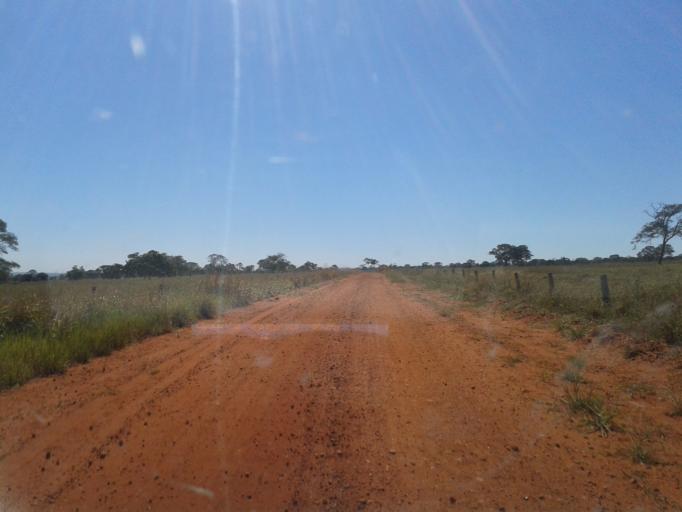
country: BR
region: Minas Gerais
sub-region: Santa Vitoria
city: Santa Vitoria
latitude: -19.0763
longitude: -50.3595
